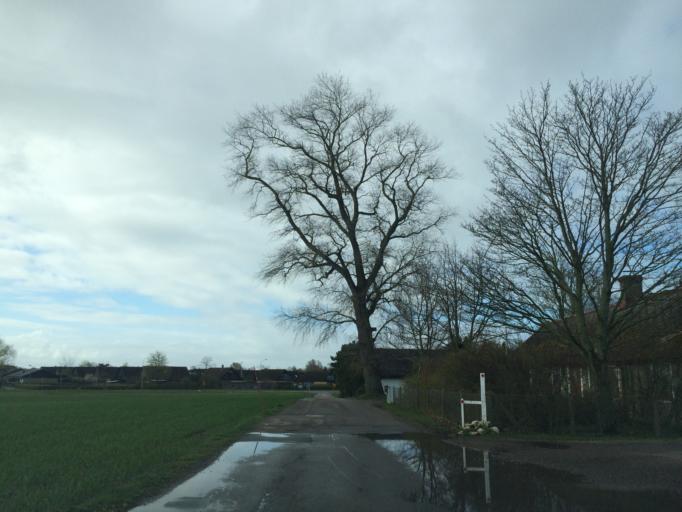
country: SE
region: Skane
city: Bjarred
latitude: 55.7335
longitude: 13.0165
